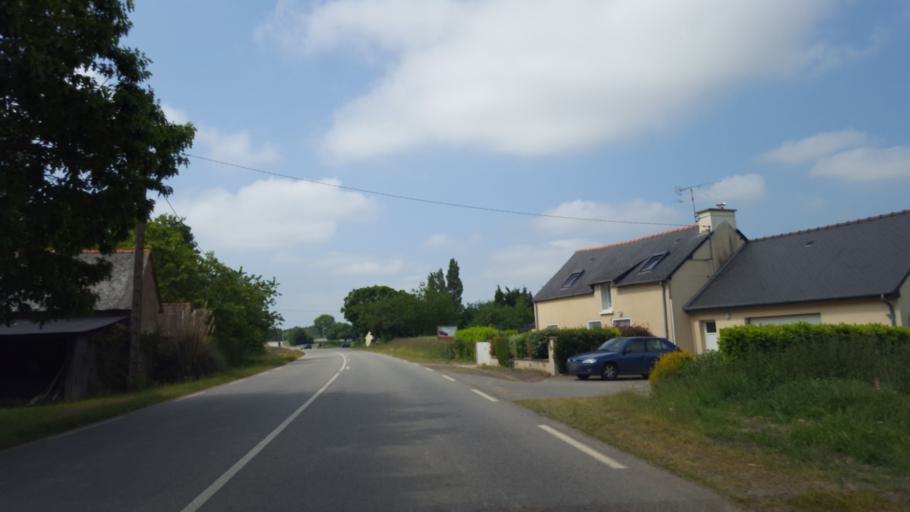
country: FR
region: Brittany
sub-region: Departement d'Ille-et-Vilaine
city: Maure-de-Bretagne
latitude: 47.9178
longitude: -1.9709
